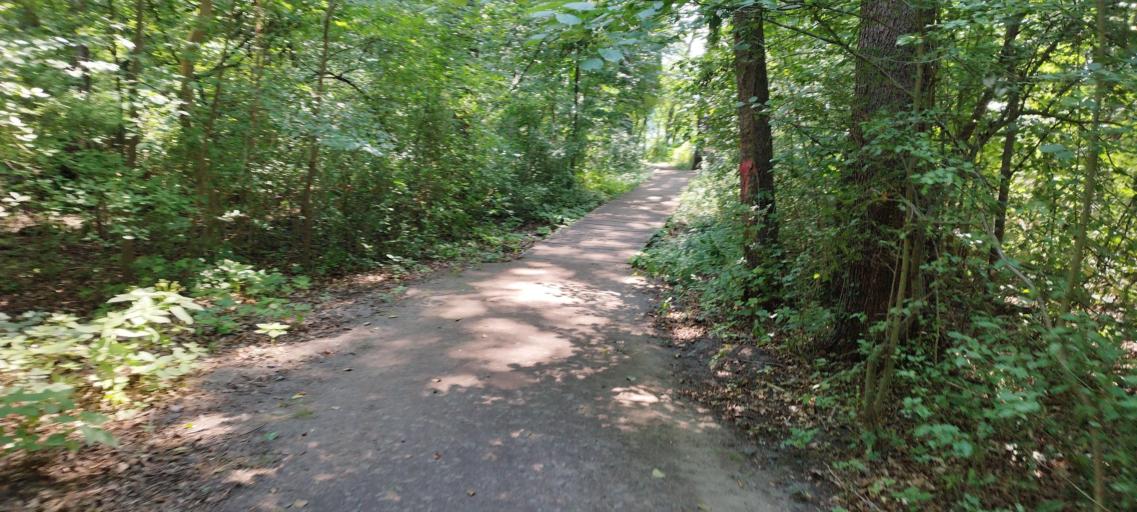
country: DE
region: Brandenburg
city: Petershagen
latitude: 52.5131
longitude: 13.8360
